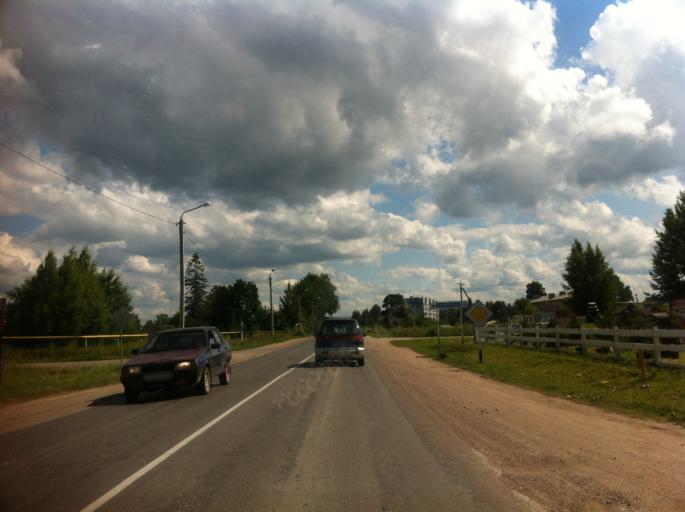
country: RU
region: Pskov
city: Pskov
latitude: 57.7971
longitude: 28.2002
